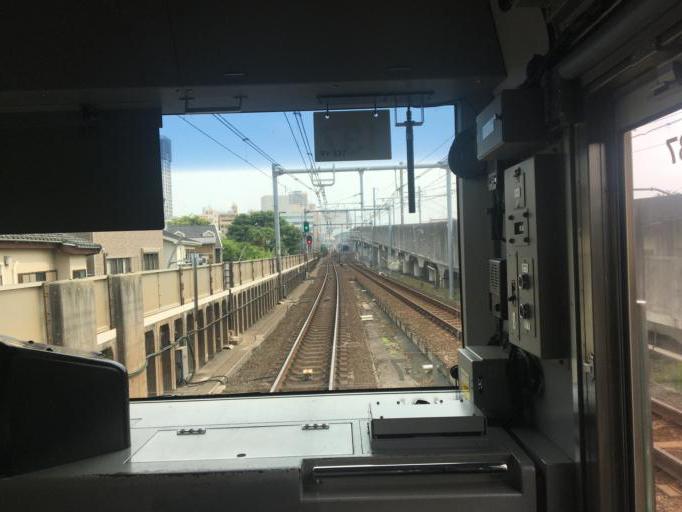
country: JP
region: Saitama
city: Soka
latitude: 35.7436
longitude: 139.8028
